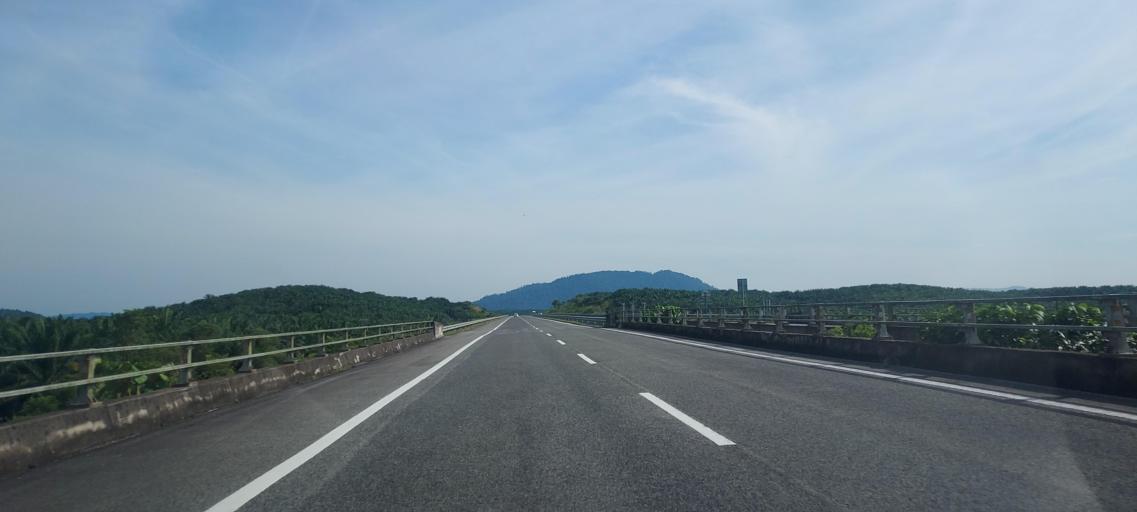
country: MY
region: Terengganu
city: Kertih
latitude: 4.5176
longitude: 103.3812
